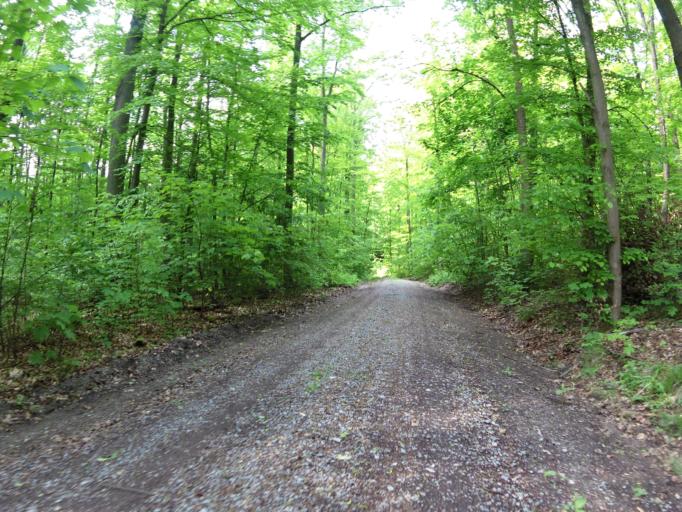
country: DE
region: Bavaria
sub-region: Regierungsbezirk Unterfranken
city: Wuerzburg
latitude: 49.7501
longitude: 9.8658
